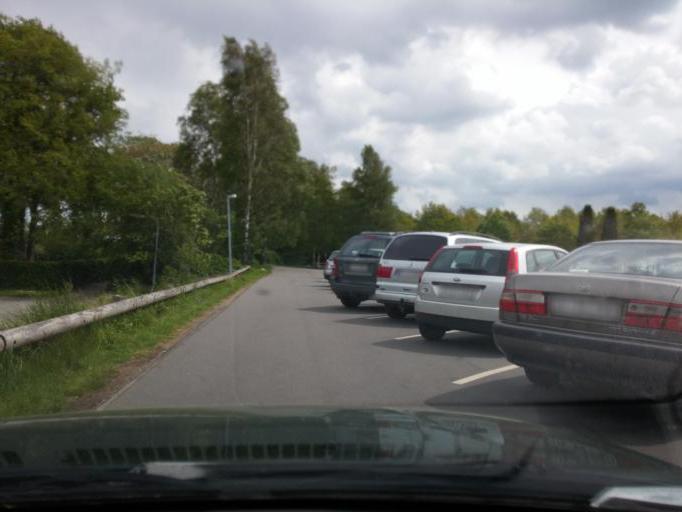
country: DK
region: South Denmark
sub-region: Odense Kommune
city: Odense
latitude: 55.4090
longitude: 10.3183
